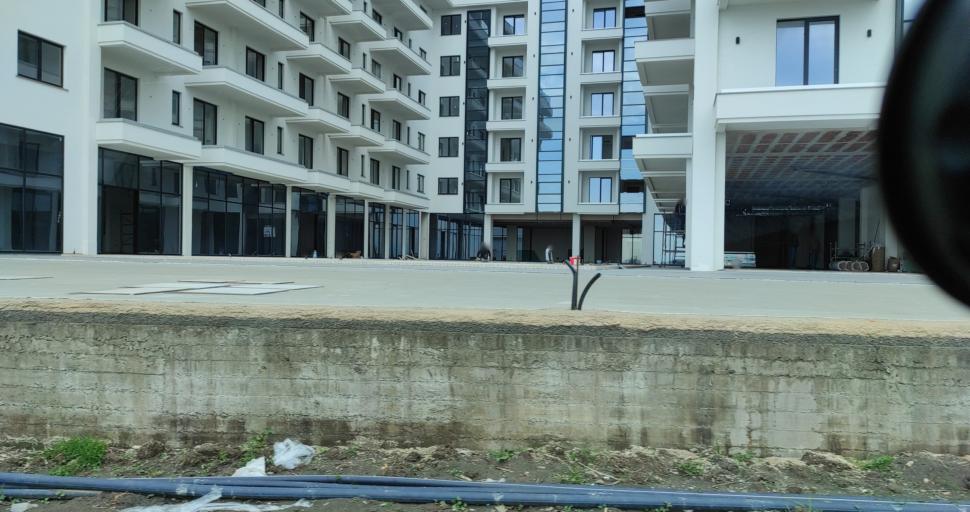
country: AL
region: Lezhe
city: Shengjin
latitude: 41.7974
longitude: 19.6016
